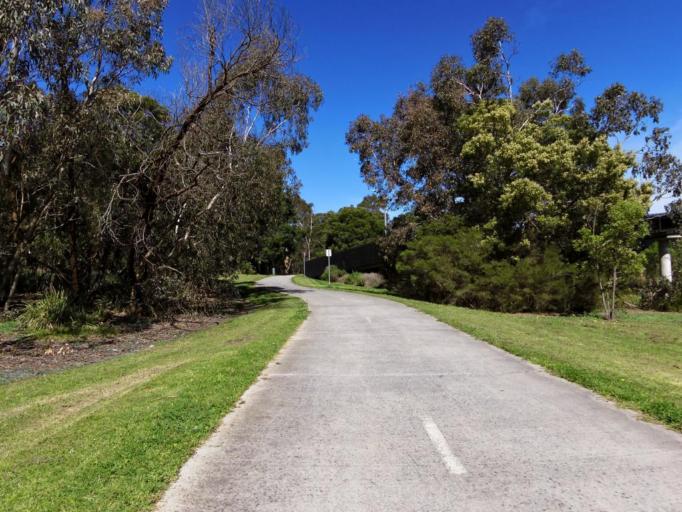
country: AU
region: Victoria
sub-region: Greater Dandenong
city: Dandenong
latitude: -37.9738
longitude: 145.1947
